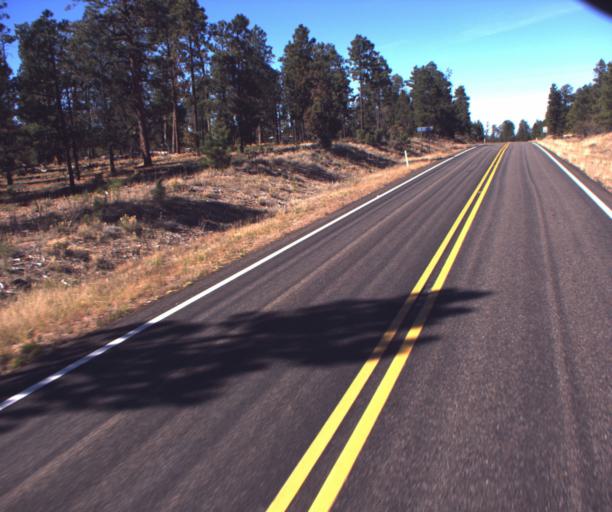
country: US
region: Arizona
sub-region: Coconino County
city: Fredonia
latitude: 36.6994
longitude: -112.2142
